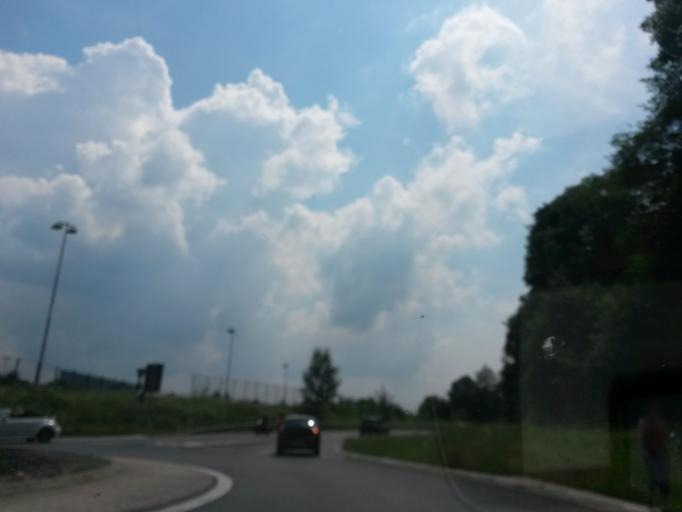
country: DE
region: North Rhine-Westphalia
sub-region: Regierungsbezirk Arnsberg
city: Olpe
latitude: 51.0776
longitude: 7.8507
